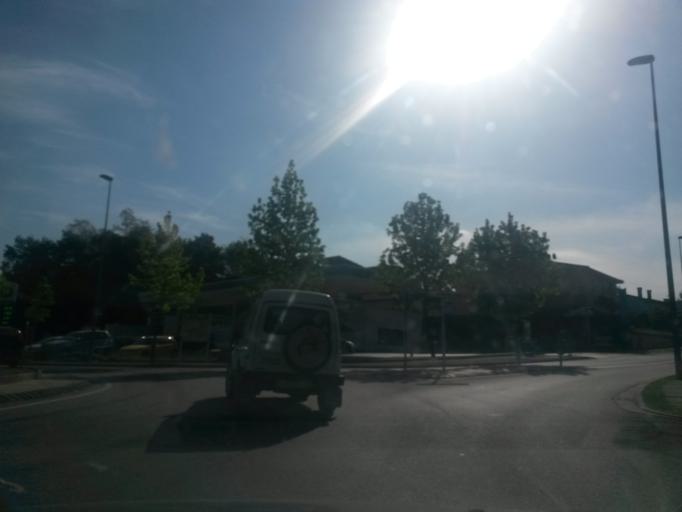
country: ES
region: Catalonia
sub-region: Provincia de Girona
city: Olot
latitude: 42.1760
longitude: 2.4913
